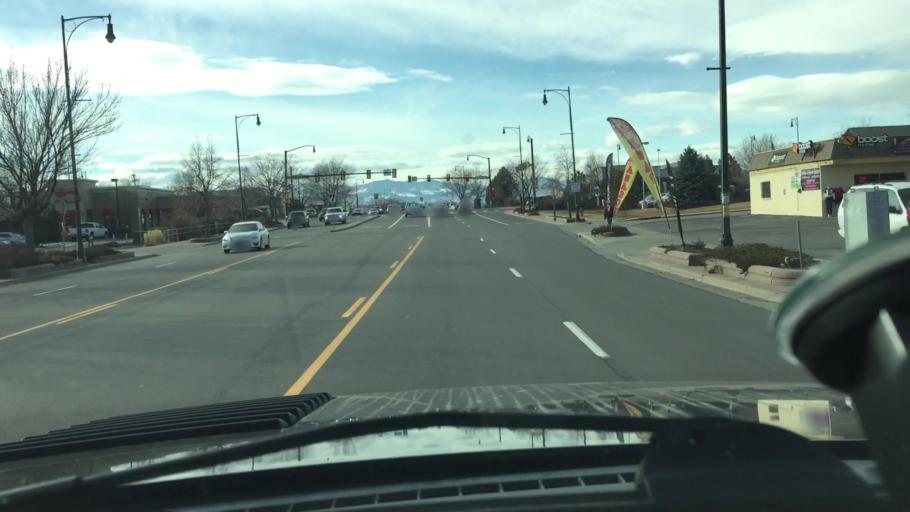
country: US
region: Colorado
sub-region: Adams County
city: Westminster
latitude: 39.8273
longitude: -105.0232
